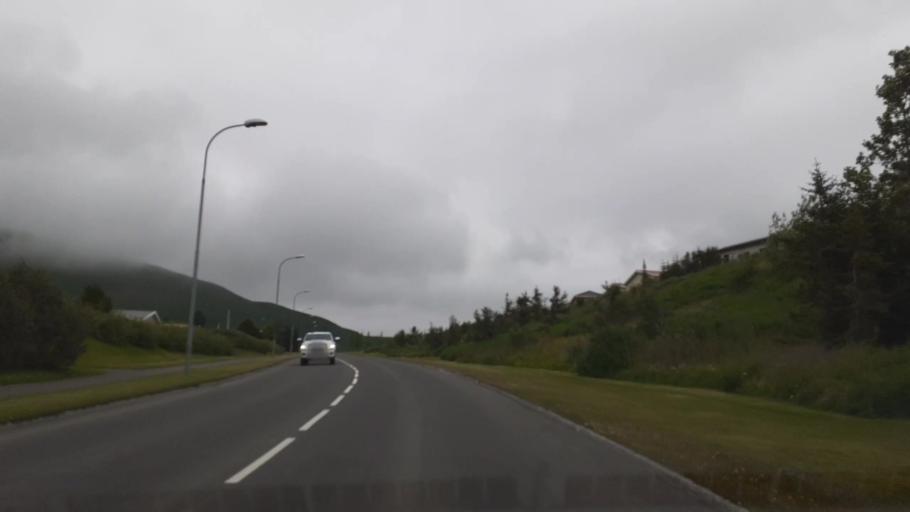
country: IS
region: Northeast
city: Husavik
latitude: 66.0370
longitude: -17.3408
